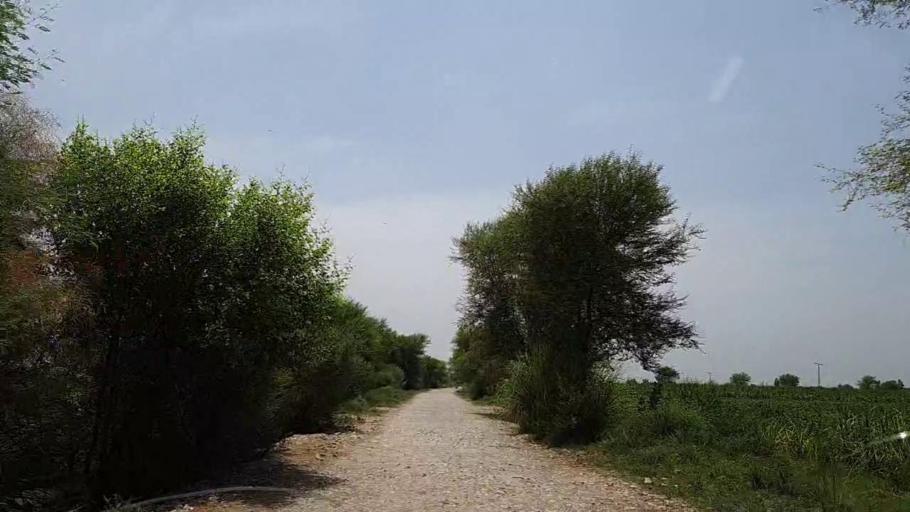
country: PK
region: Sindh
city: Khanpur
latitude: 27.8364
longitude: 69.4840
